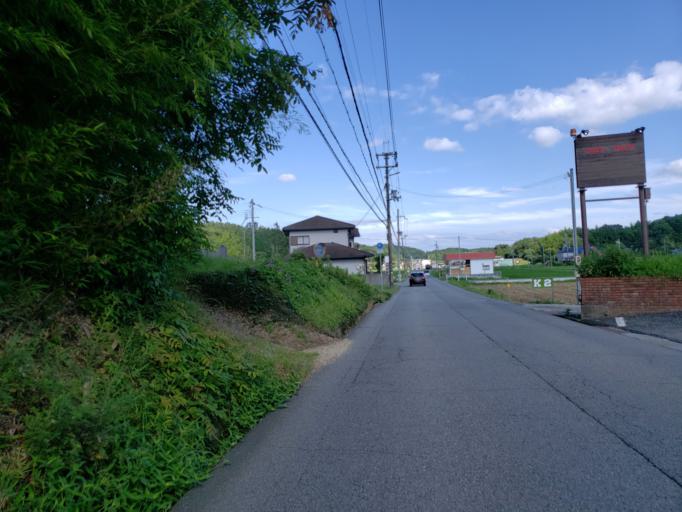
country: JP
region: Hyogo
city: Himeji
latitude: 34.9077
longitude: 134.7850
